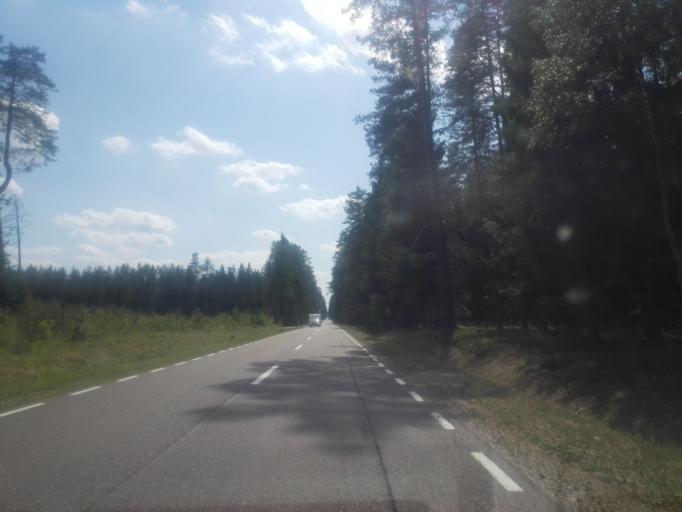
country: PL
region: Podlasie
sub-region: Powiat augustowski
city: Augustow
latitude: 53.9217
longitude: 23.1529
